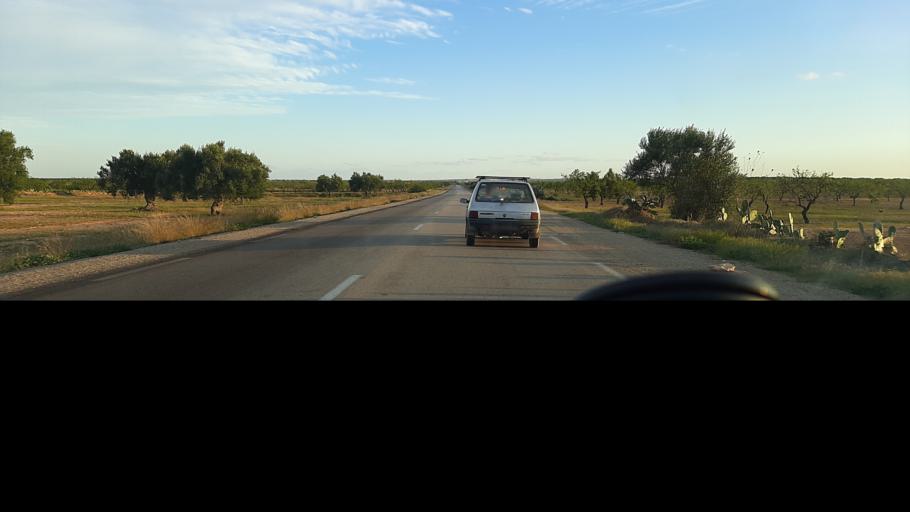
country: TN
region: Safaqis
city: Sfax
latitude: 34.9182
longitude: 10.6289
